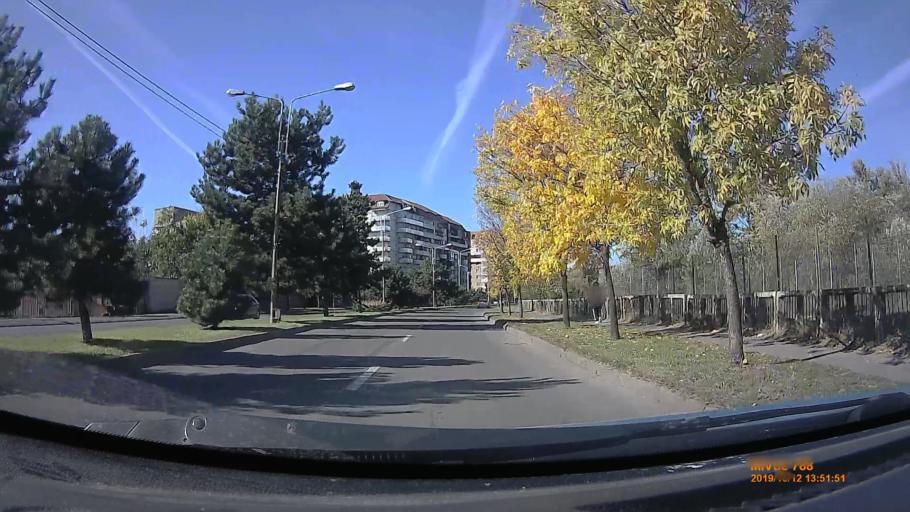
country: RO
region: Bihor
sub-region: Comuna Biharea
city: Oradea
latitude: 47.0473
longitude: 21.9637
